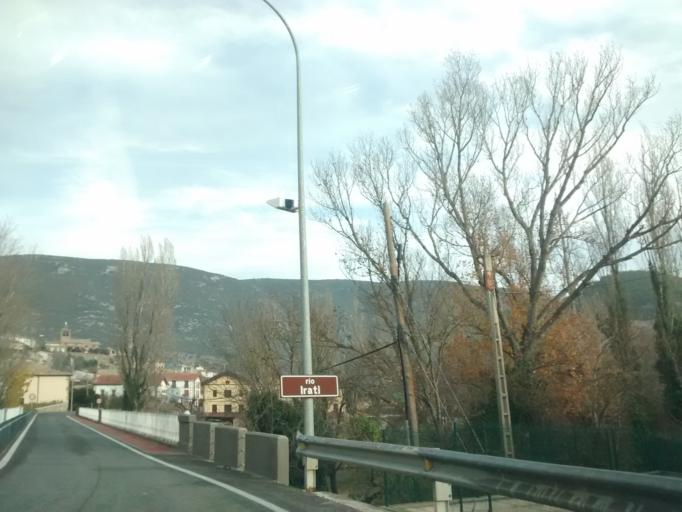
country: ES
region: Navarre
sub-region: Provincia de Navarra
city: Liedena
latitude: 42.6146
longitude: -1.2769
